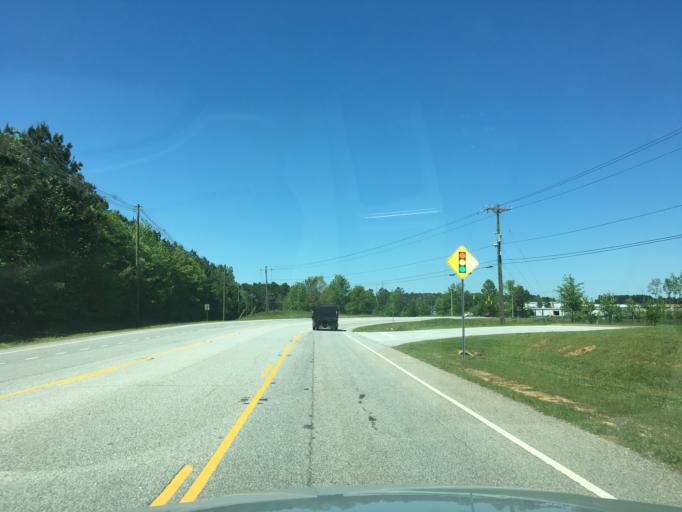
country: US
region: South Carolina
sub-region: Greenville County
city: Greer
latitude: 34.8895
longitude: -82.1962
